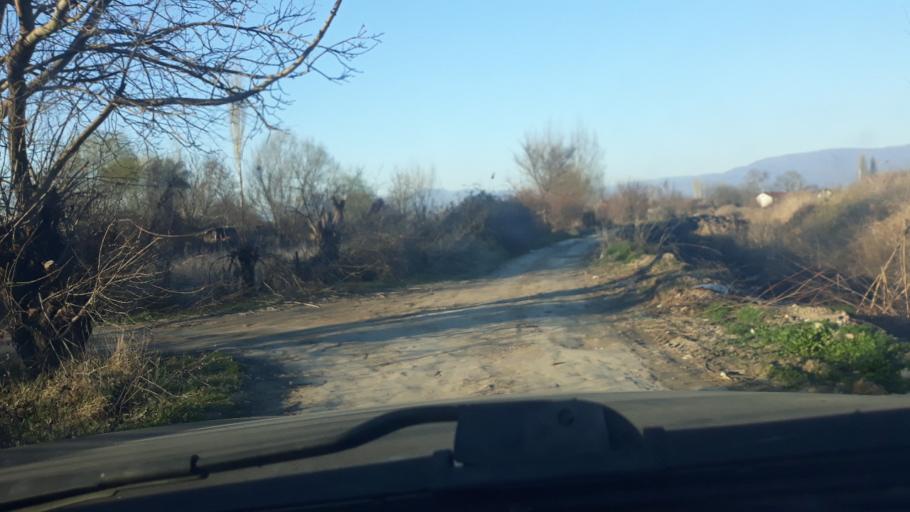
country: MK
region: Strumica
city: Strumica
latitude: 41.4424
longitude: 22.6264
